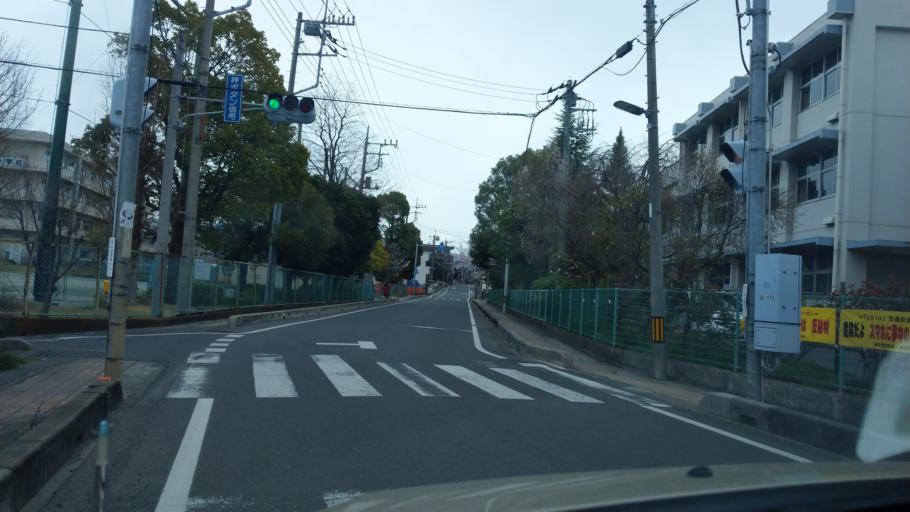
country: JP
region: Saitama
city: Yono
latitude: 35.8661
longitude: 139.6342
